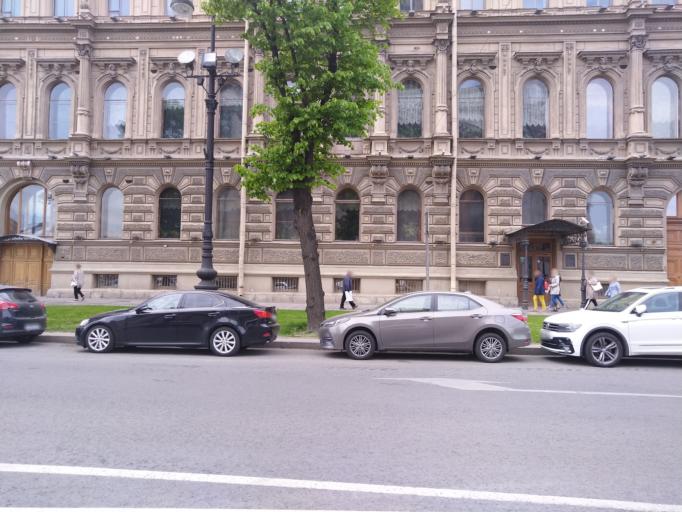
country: RU
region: St.-Petersburg
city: Saint Petersburg
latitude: 59.9337
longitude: 30.3050
